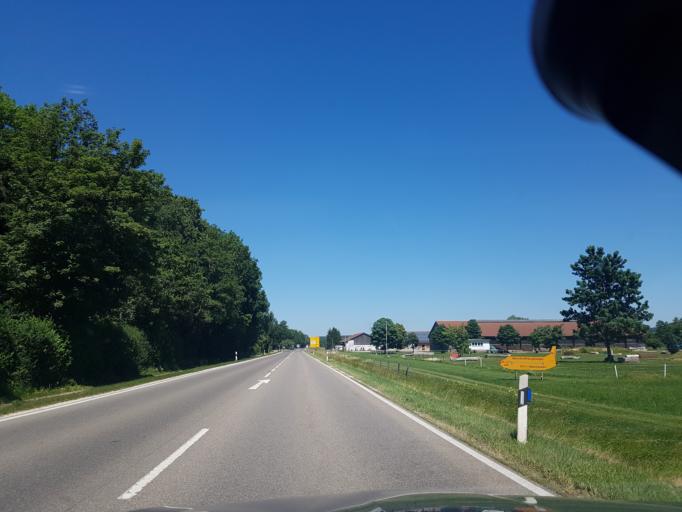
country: DE
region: Bavaria
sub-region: Swabia
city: Weissenhorn
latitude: 48.2926
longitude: 10.1363
